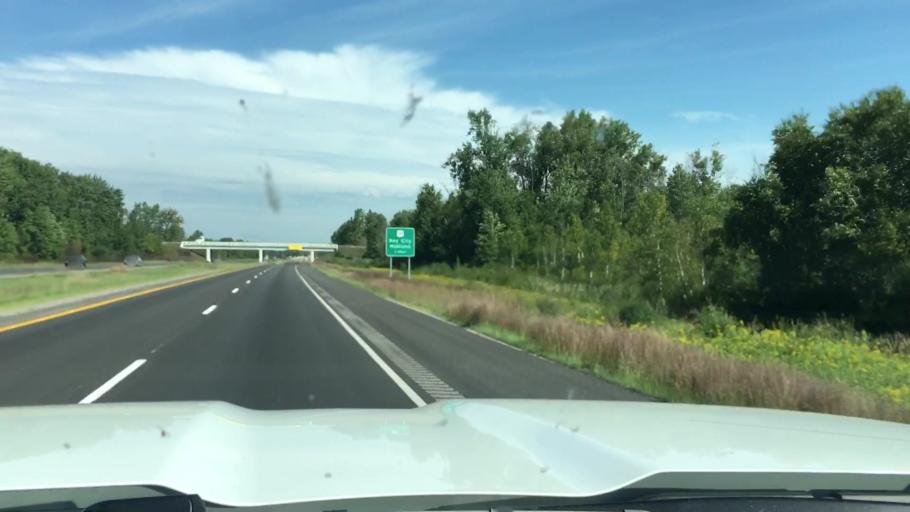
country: US
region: Michigan
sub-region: Saginaw County
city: Freeland
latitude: 43.5798
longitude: -84.1394
